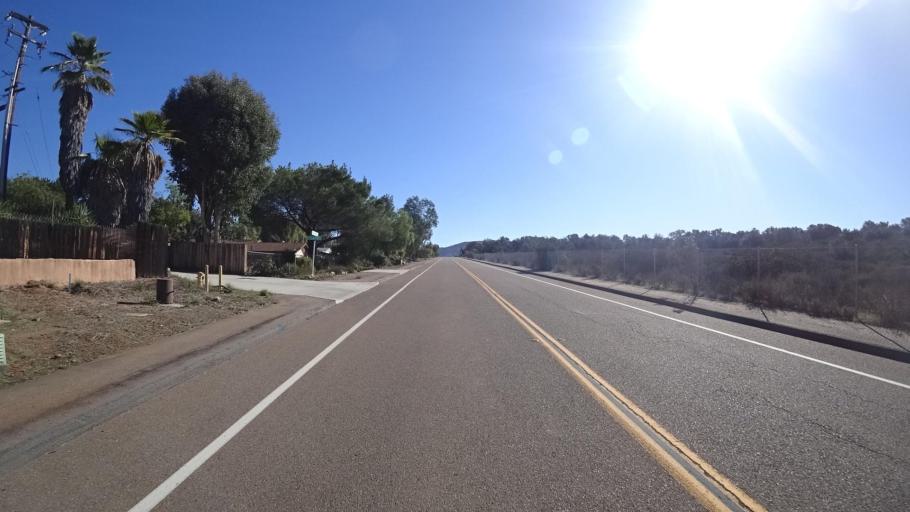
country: US
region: California
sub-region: San Diego County
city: Jamul
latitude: 32.7221
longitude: -116.8669
